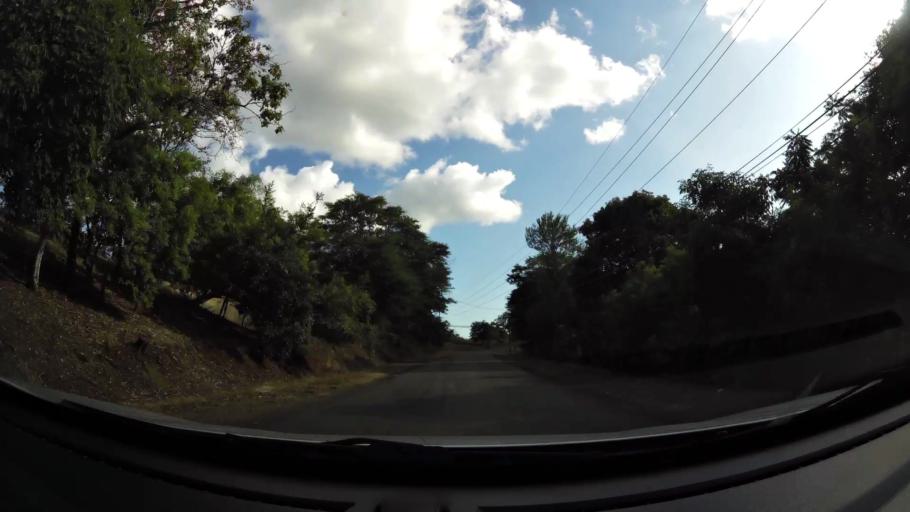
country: CR
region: Guanacaste
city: Sardinal
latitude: 10.5595
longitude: -85.6810
